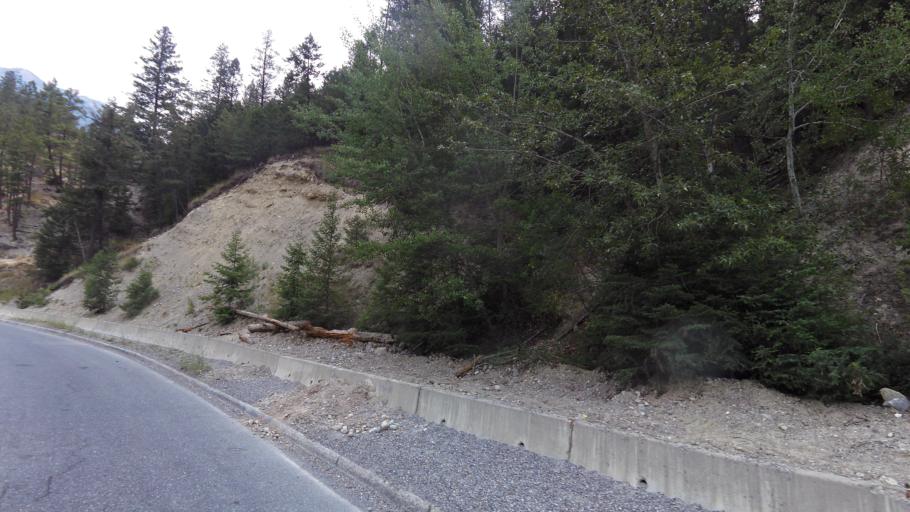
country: CA
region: British Columbia
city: Invermere
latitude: 50.6319
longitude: -116.0573
